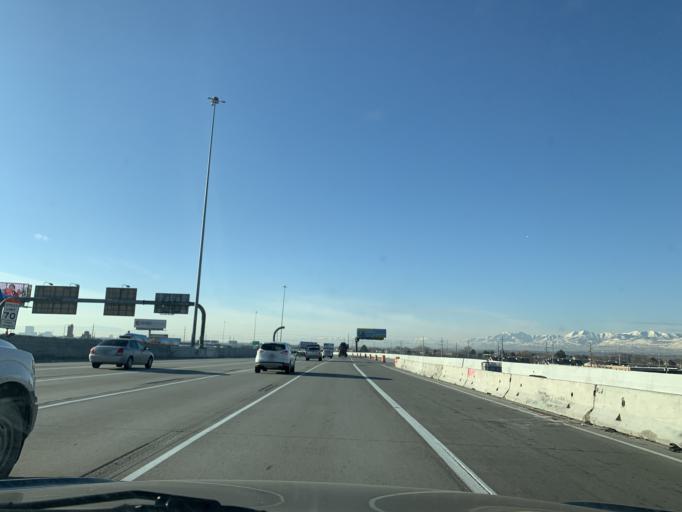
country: US
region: Utah
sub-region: Salt Lake County
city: Centerfield
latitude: 40.6942
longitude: -111.9031
